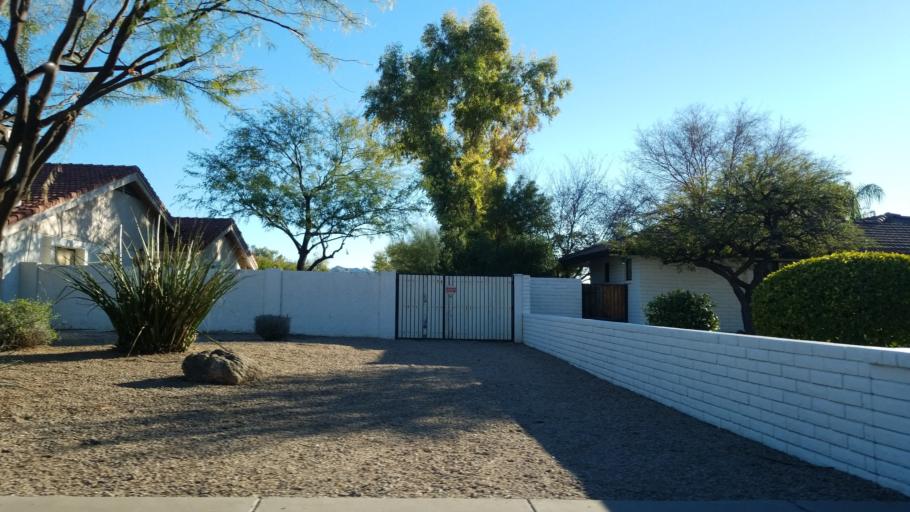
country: US
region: Arizona
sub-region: Maricopa County
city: Paradise Valley
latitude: 33.5939
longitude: -111.9670
